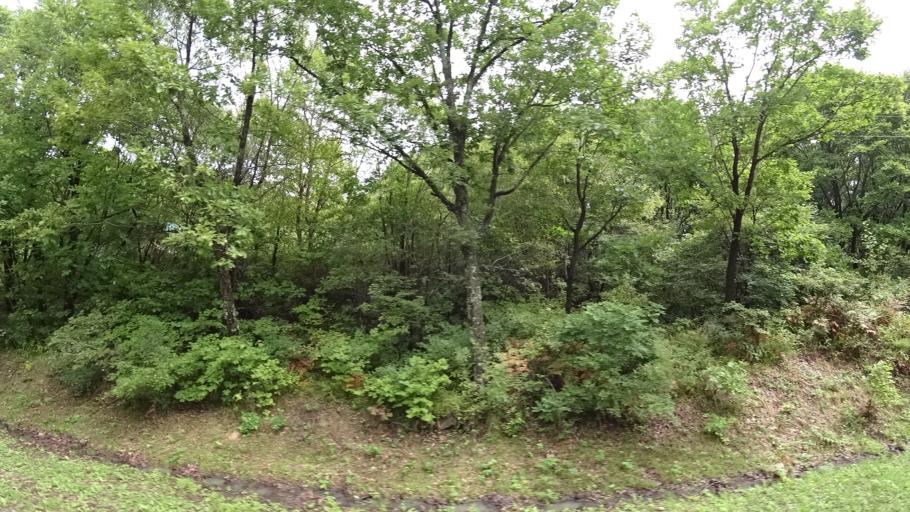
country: RU
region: Primorskiy
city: Monastyrishche
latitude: 44.1687
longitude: 132.5386
